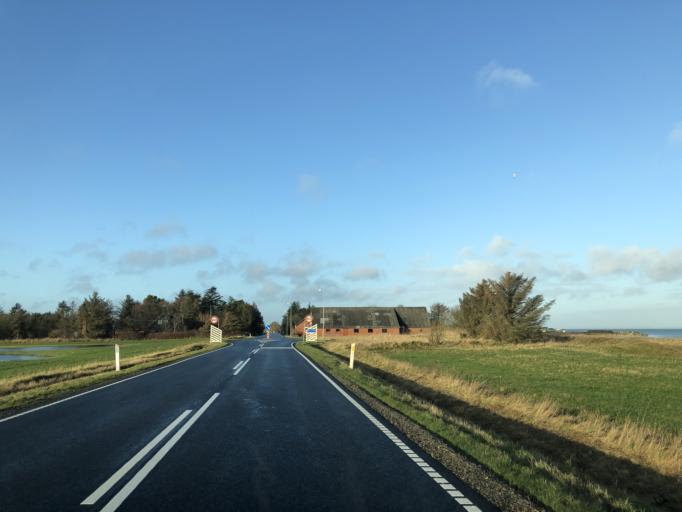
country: DK
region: Central Jutland
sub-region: Struer Kommune
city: Struer
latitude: 56.5443
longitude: 8.4989
